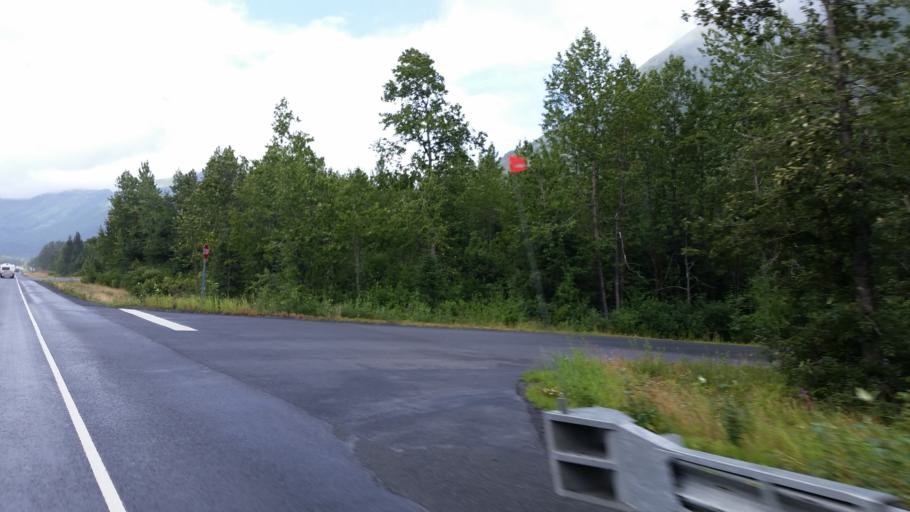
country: US
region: Alaska
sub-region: Anchorage Municipality
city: Girdwood
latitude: 60.7504
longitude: -149.2515
